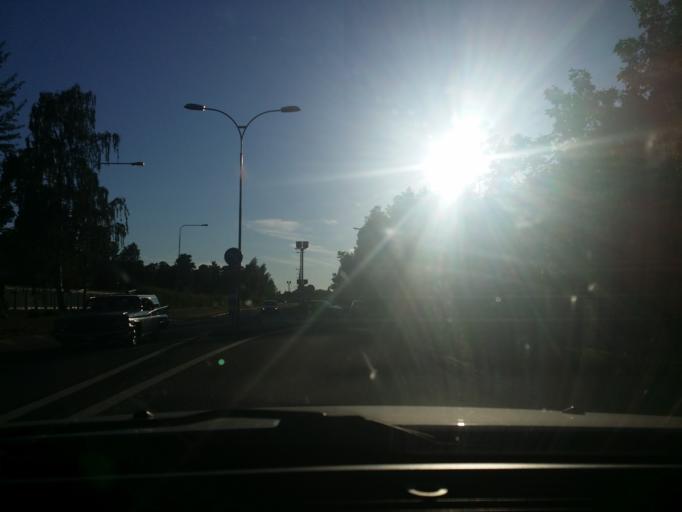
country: SE
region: Vaestmanland
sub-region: Vasteras
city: Vasteras
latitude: 59.6146
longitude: 16.5897
